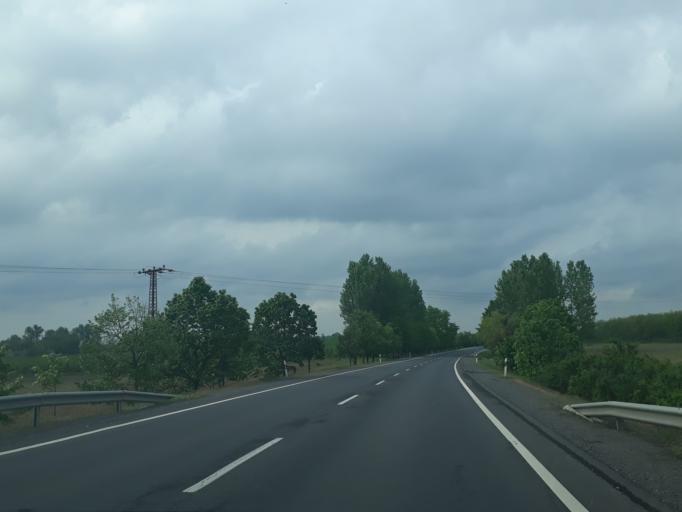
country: HU
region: Szabolcs-Szatmar-Bereg
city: Ajak
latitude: 48.1878
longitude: 22.0417
